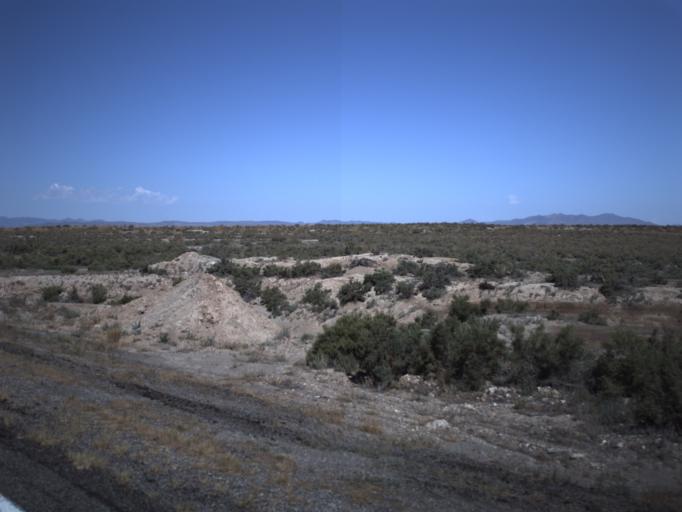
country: US
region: Utah
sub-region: Millard County
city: Delta
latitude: 39.3308
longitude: -112.7164
